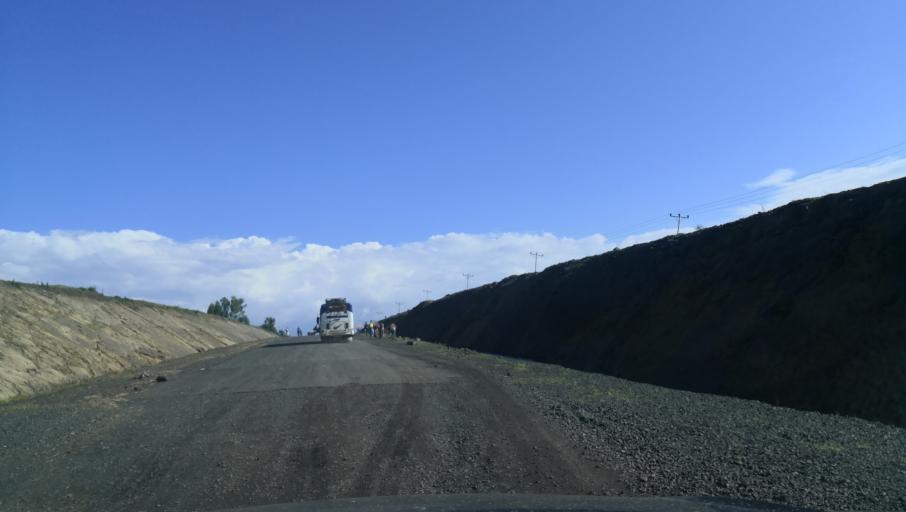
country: ET
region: Oromiya
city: Tulu Bolo
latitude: 8.6321
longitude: 38.2321
